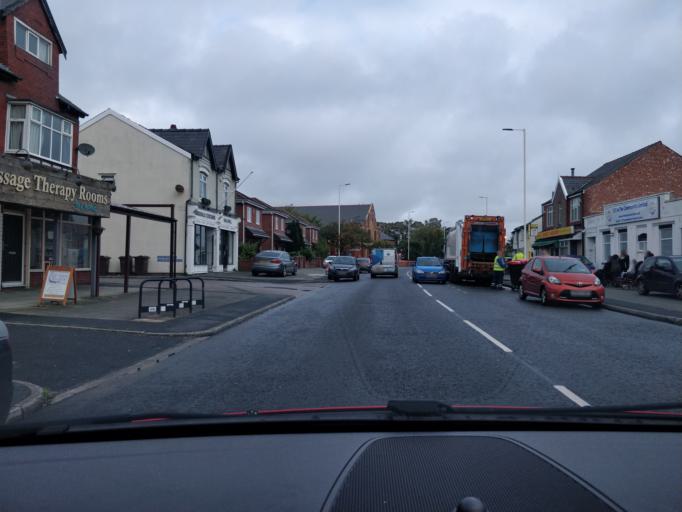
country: GB
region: England
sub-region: Sefton
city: Southport
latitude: 53.6194
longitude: -3.0155
